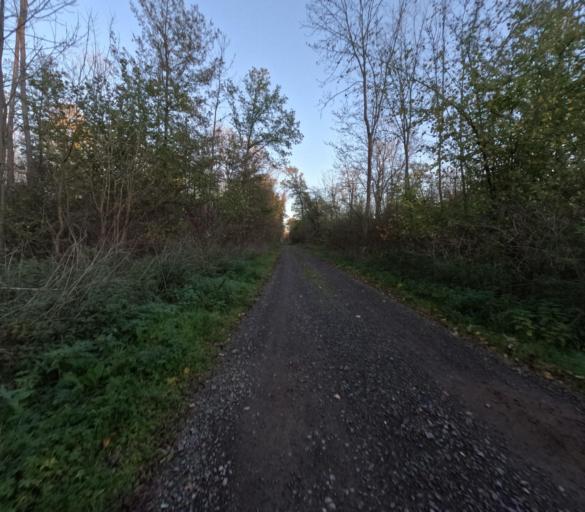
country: DE
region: Saxony
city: Schkeuditz
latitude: 51.3804
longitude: 12.2261
